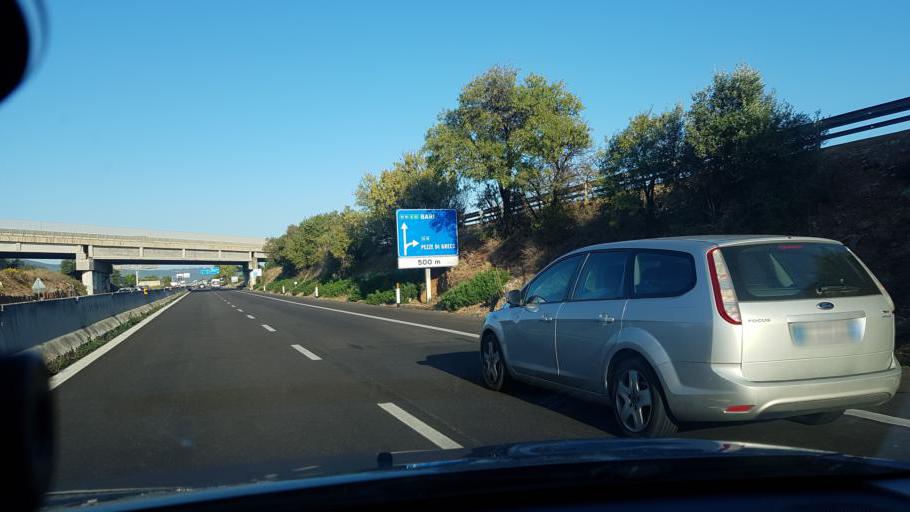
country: IT
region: Apulia
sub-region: Provincia di Brindisi
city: Fasano
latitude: 40.8354
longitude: 17.3885
